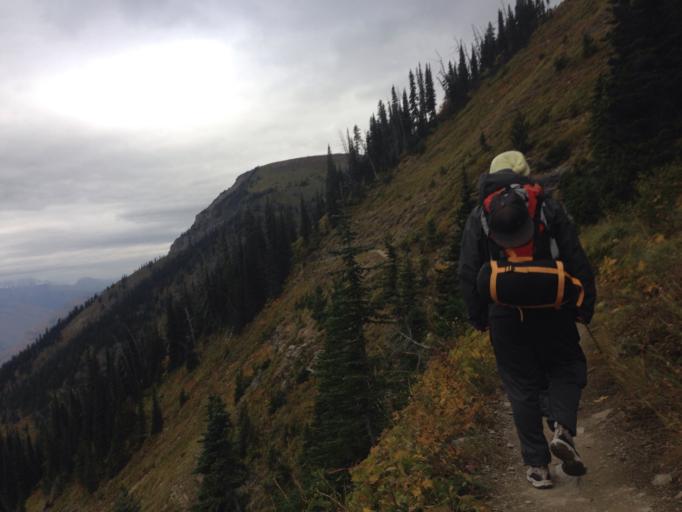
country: US
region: Montana
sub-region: Flathead County
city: Columbia Falls
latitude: 48.7210
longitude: -113.7203
